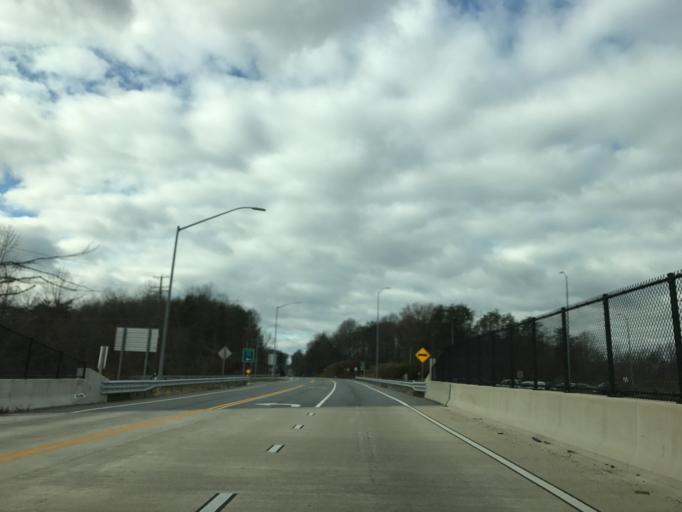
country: US
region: Pennsylvania
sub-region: York County
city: New Freedom
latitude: 39.6326
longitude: -76.6721
